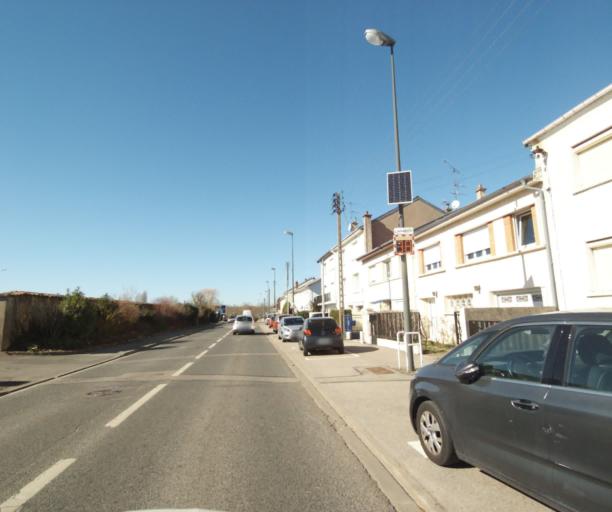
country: FR
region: Lorraine
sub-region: Departement de Meurthe-et-Moselle
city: Jarville-la-Malgrange
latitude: 48.6668
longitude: 6.1944
